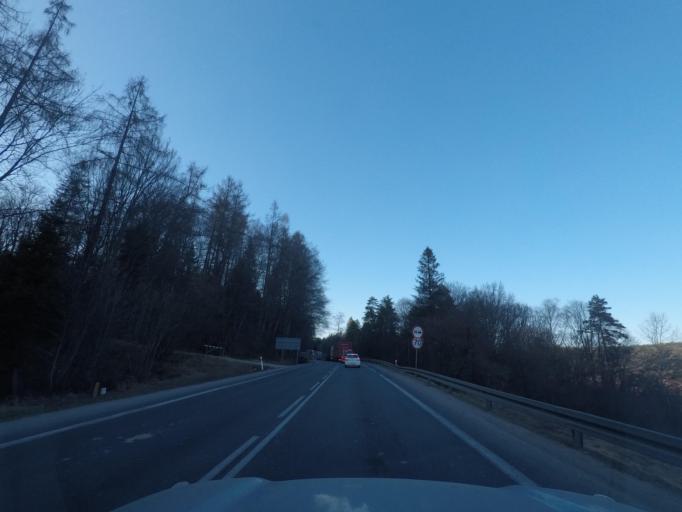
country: PL
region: Subcarpathian Voivodeship
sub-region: Powiat krosnienski
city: Dukla
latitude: 49.4775
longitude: 21.7081
